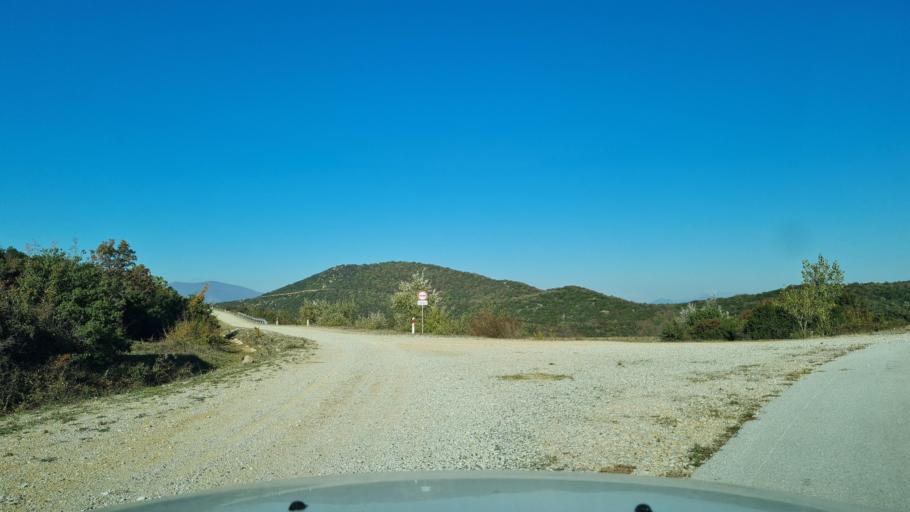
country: MK
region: Bogdanci
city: Bogdanci
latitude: 41.2220
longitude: 22.5516
